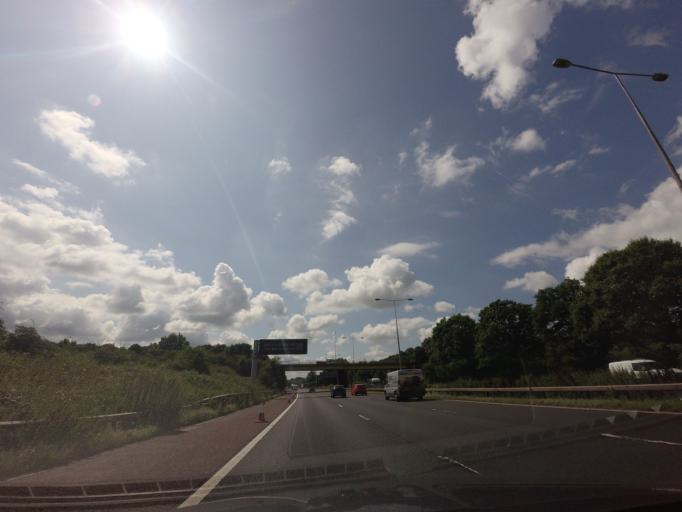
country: GB
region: England
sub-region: Lancashire
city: Clayton-le-Woods
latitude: 53.7071
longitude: -2.6752
